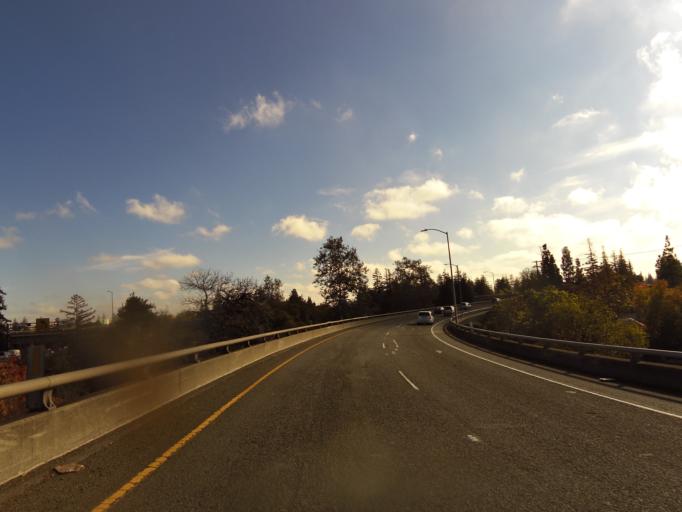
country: US
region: California
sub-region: Sacramento County
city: Sacramento
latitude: 38.5586
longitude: -121.4758
